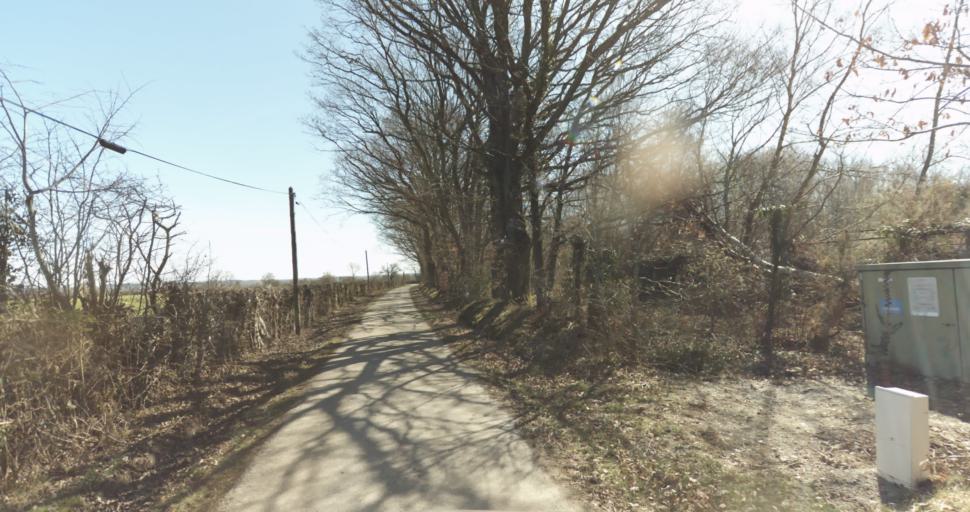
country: FR
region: Lower Normandy
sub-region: Departement du Calvados
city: Livarot
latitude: 48.9927
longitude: 0.1104
